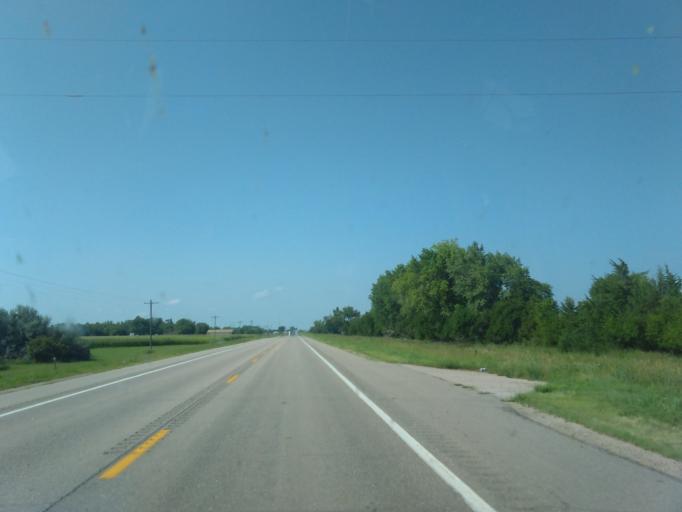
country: US
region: Nebraska
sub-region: Buffalo County
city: Gibbon
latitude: 40.6743
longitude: -98.9515
